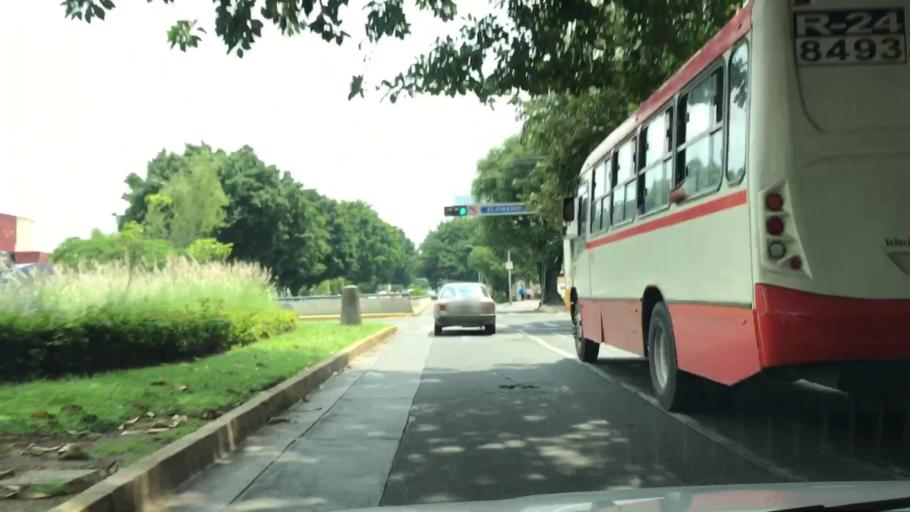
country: MX
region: Jalisco
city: Guadalajara
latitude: 20.6923
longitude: -103.3757
